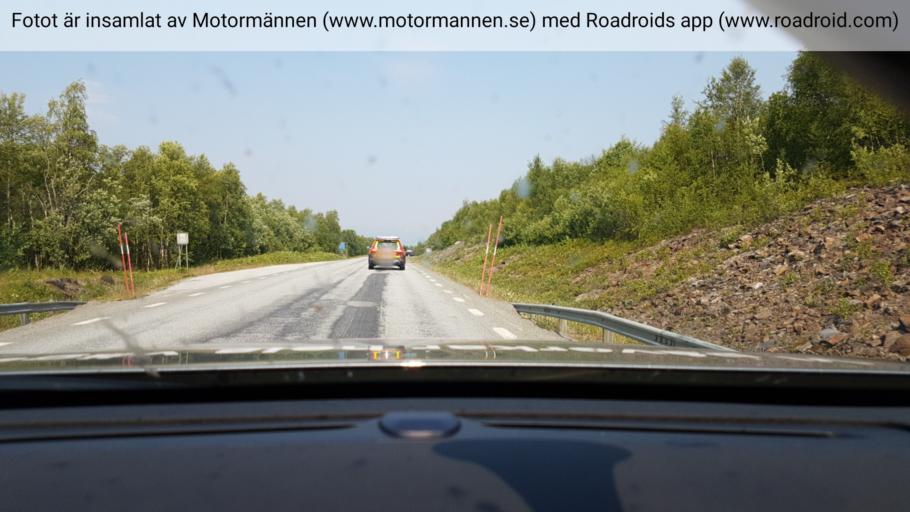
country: NO
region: Nordland
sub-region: Rana
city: Mo i Rana
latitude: 65.7817
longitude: 15.1117
